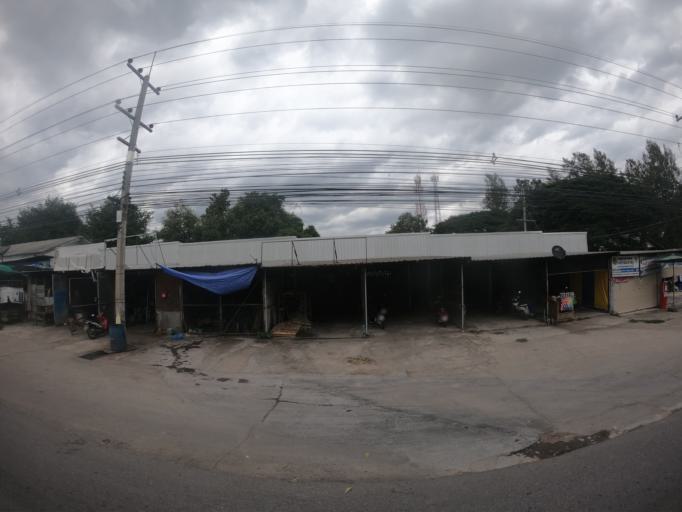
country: TH
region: Nakhon Ratchasima
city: Nakhon Ratchasima
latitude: 14.8880
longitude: 102.1685
